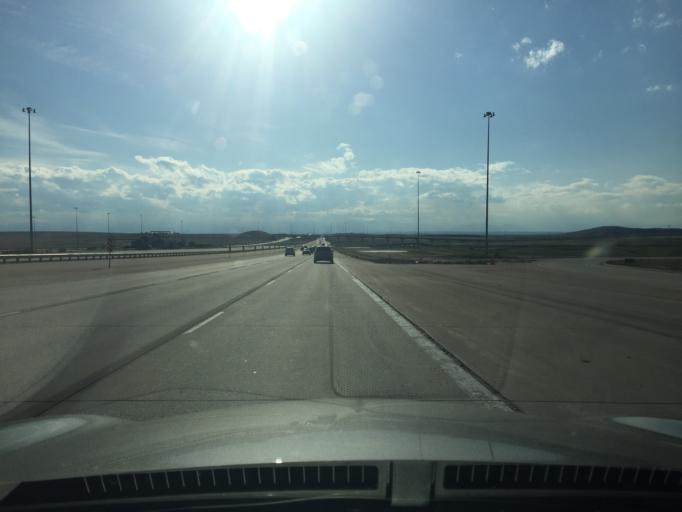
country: US
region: Colorado
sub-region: Adams County
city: Aurora
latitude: 39.8345
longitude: -104.7187
